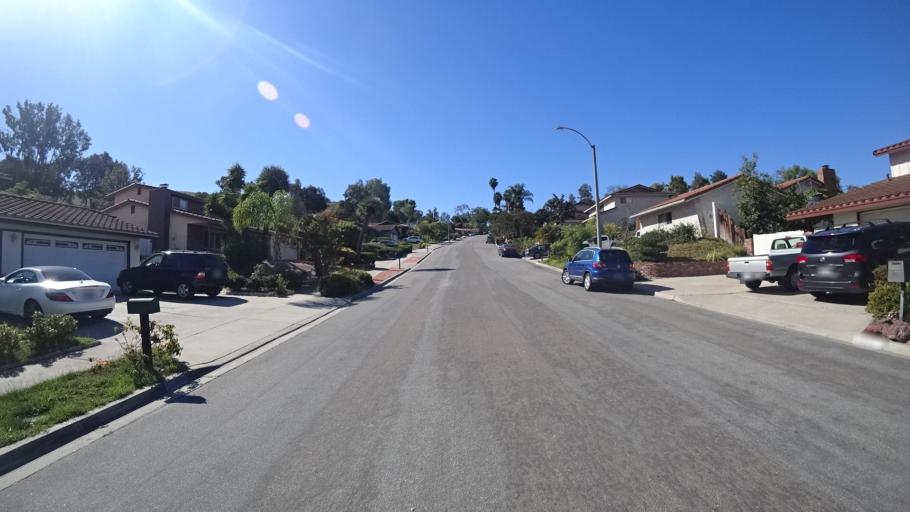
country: US
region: California
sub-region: San Diego County
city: Bonita
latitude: 32.6682
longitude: -117.0085
